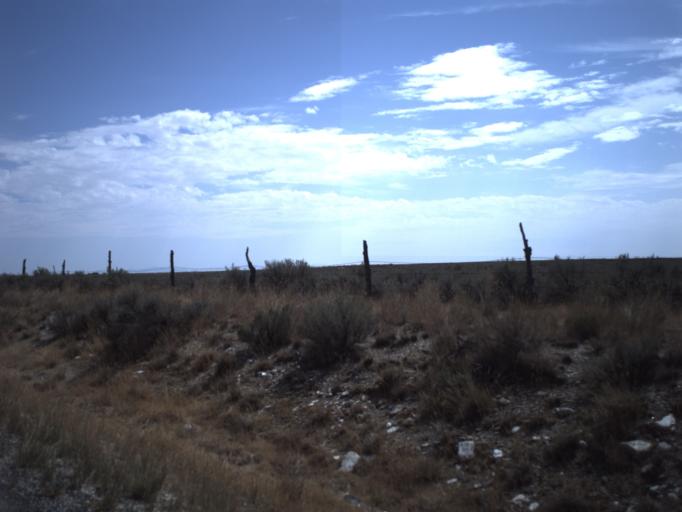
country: US
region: Idaho
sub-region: Cassia County
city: Burley
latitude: 41.8153
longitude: -113.2224
